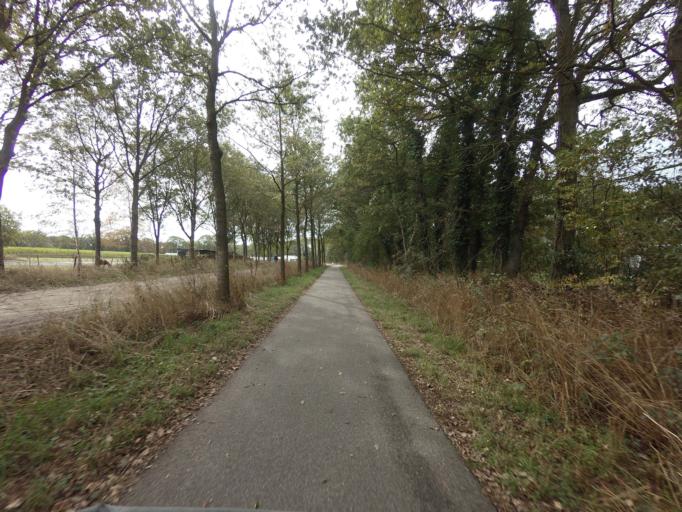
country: NL
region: Drenthe
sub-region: Gemeente Tynaarlo
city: Vries
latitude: 53.0711
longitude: 6.4639
